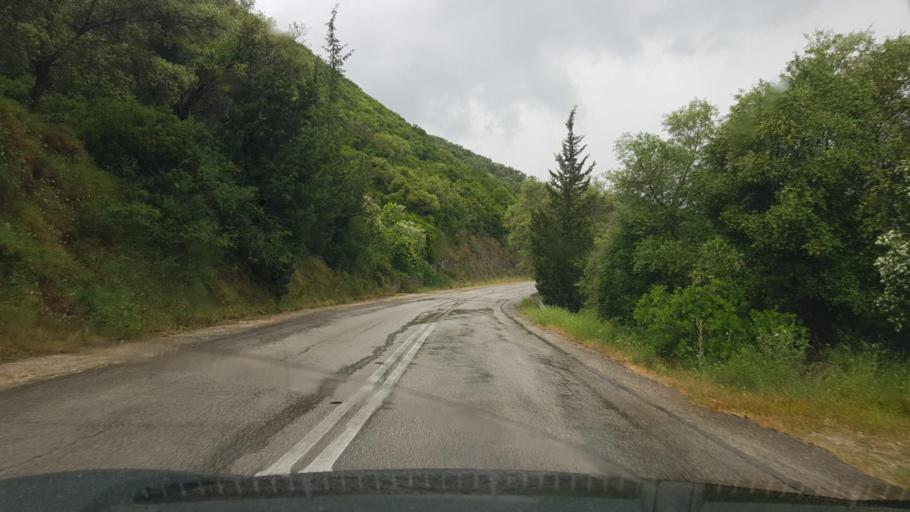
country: GR
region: Ionian Islands
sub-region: Lefkada
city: Nidri
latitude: 38.6330
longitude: 20.6635
